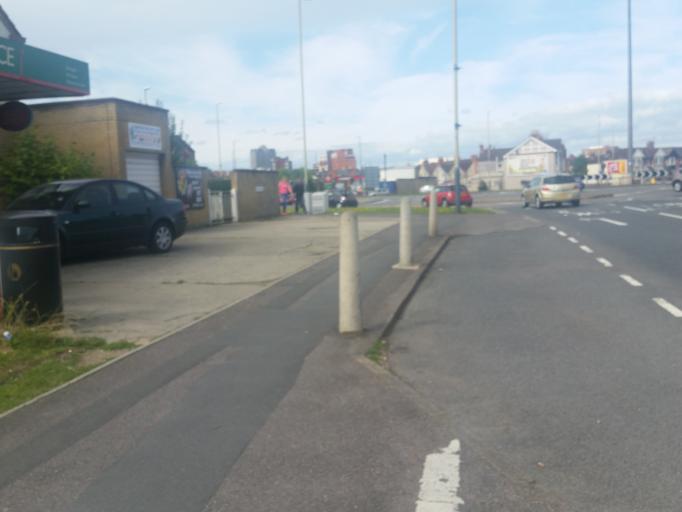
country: GB
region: England
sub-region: Borough of Swindon
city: Swindon
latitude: 51.5625
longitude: -1.7703
